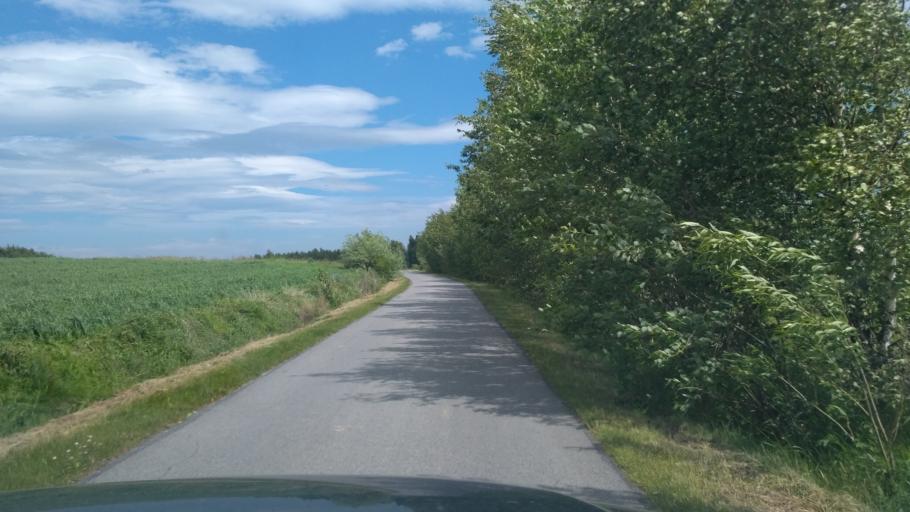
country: PL
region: Subcarpathian Voivodeship
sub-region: Powiat ropczycko-sedziszowski
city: Zagorzyce
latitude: 49.9759
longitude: 21.6561
